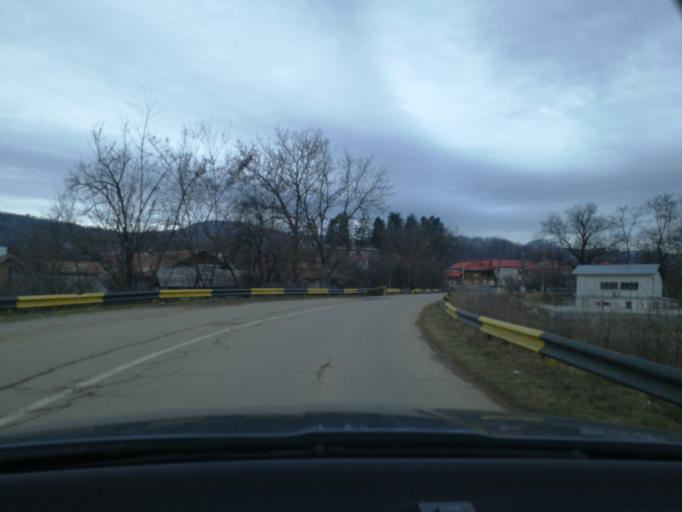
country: RO
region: Prahova
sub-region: Comuna Adunati
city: Ocina de Sus
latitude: 45.1820
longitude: 25.6002
